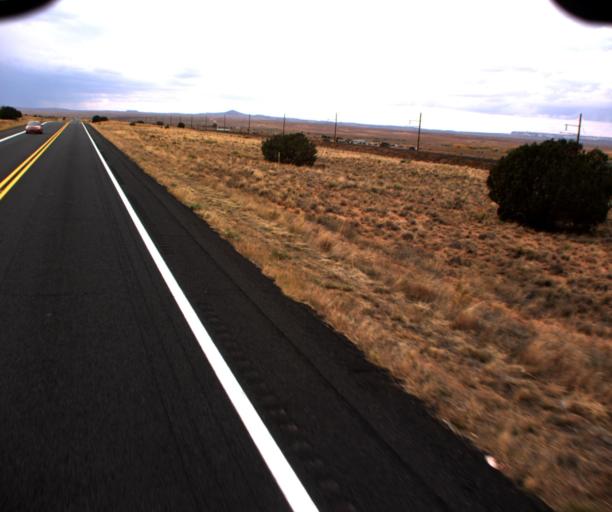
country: US
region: Arizona
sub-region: Coconino County
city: Kaibito
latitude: 36.4059
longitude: -110.8410
